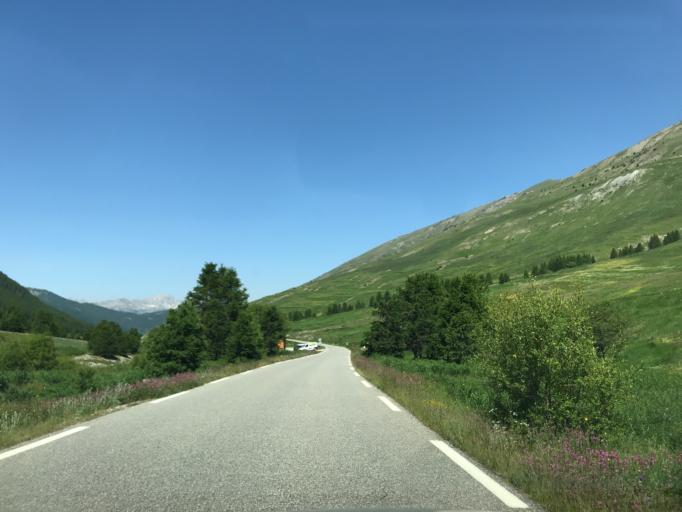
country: IT
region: Piedmont
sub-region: Provincia di Cuneo
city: Pontechianale
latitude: 44.7183
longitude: 6.9062
